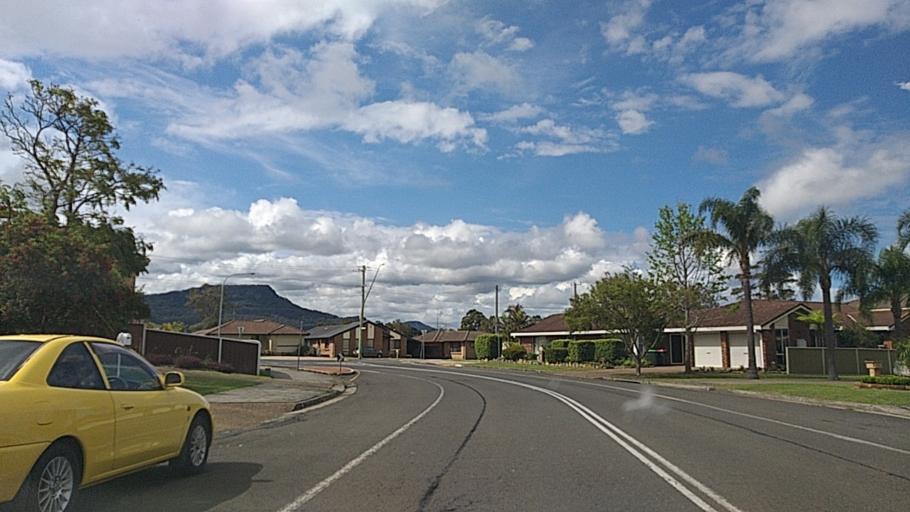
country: AU
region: New South Wales
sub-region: Wollongong
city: Dapto
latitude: -34.4922
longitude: 150.7823
